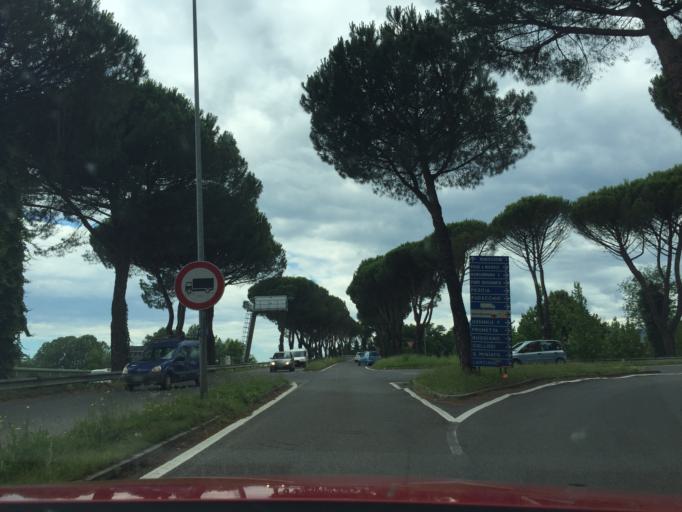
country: IT
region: Tuscany
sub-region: Provincia di Pistoia
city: Pieve a Nievole
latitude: 43.8771
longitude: 10.7904
